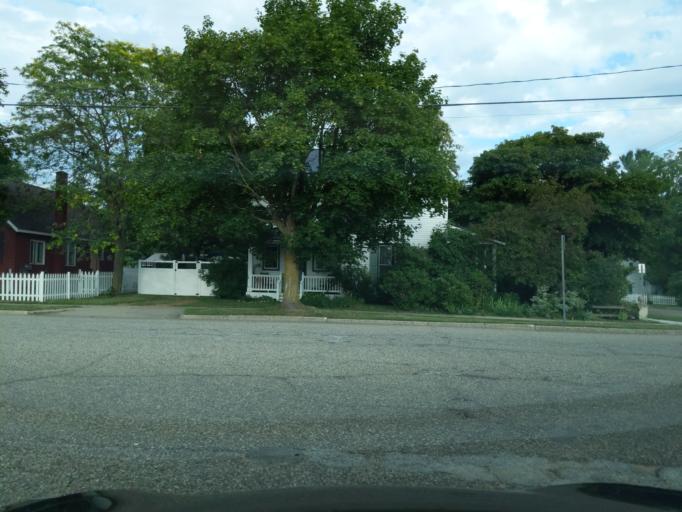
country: US
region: Michigan
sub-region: Clare County
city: Clare
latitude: 43.8208
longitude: -84.7665
